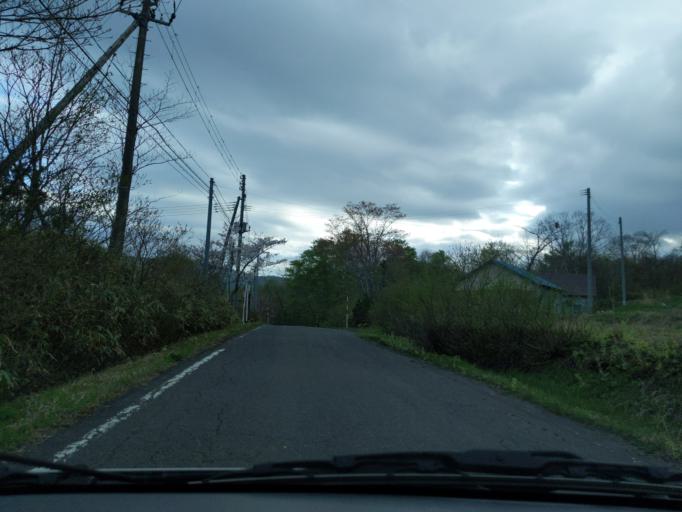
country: JP
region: Iwate
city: Ichinoseki
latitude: 38.9263
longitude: 140.8276
